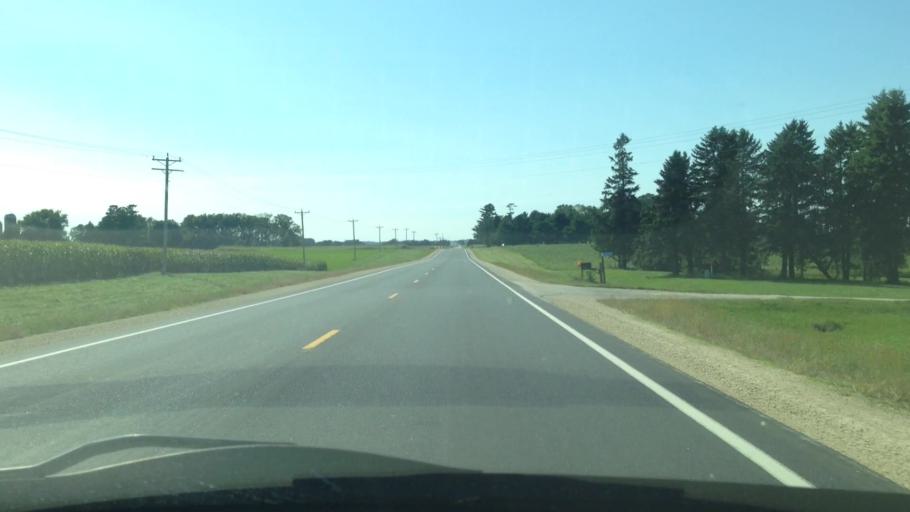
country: US
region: Minnesota
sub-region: Winona County
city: Lewiston
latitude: 43.9697
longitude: -91.8476
